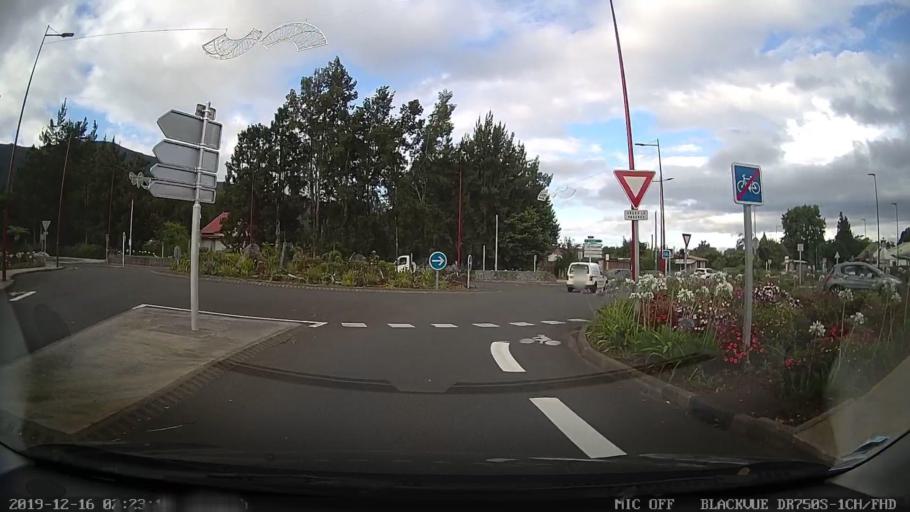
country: RE
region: Reunion
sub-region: Reunion
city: Salazie
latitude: -21.1433
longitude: 55.6204
